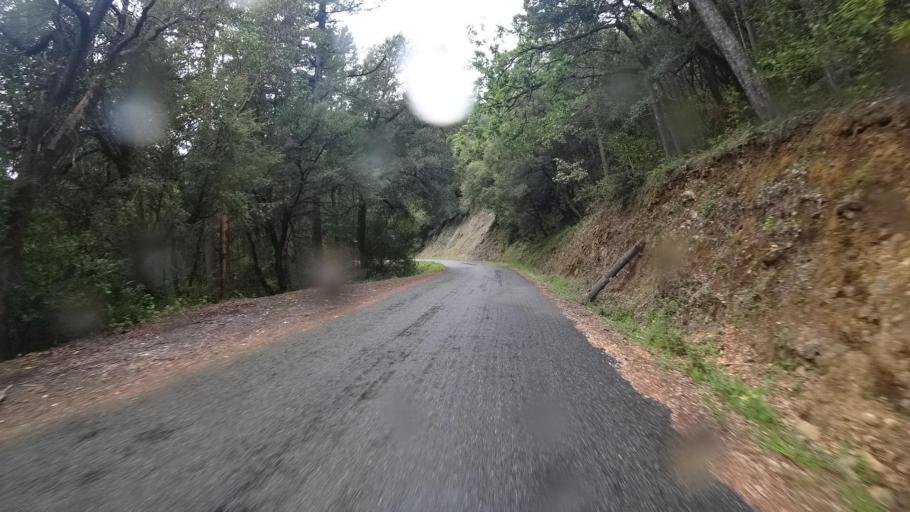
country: US
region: California
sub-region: Siskiyou County
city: Happy Camp
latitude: 41.3722
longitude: -123.5019
